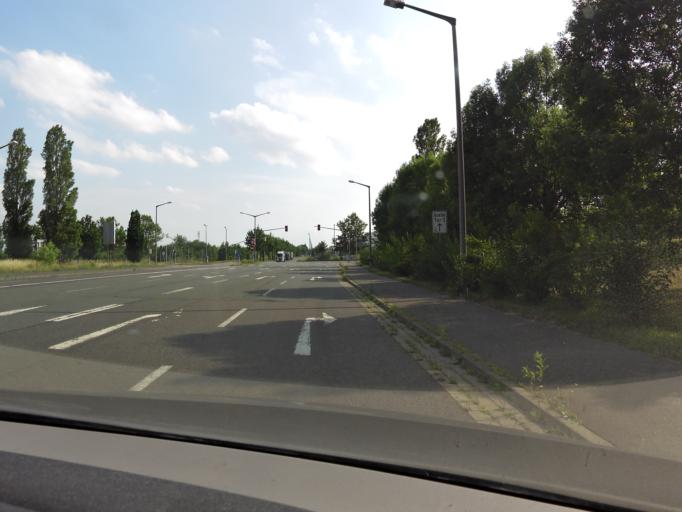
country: DE
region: Saxony
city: Rackwitz
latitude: 51.3941
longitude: 12.4124
